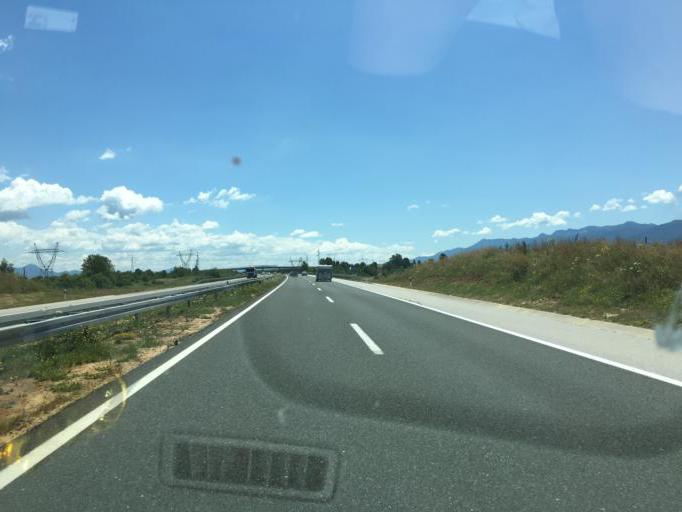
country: HR
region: Licko-Senjska
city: Gospic
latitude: 44.5310
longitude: 15.4473
